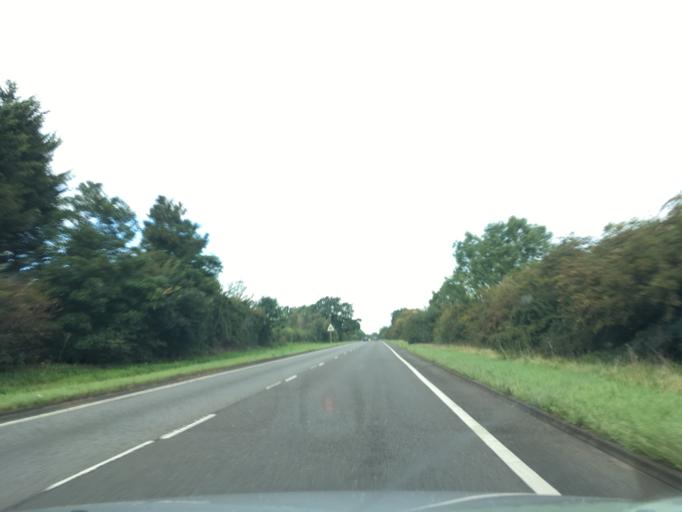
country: GB
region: England
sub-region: Oxfordshire
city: Oxford
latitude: 51.7791
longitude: -1.2380
